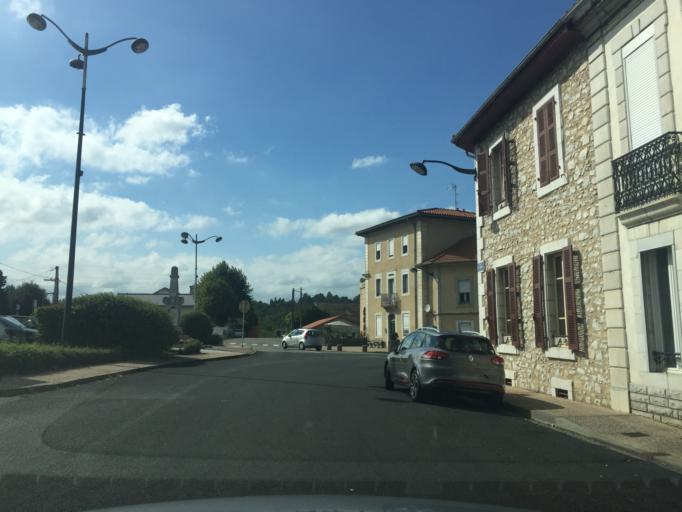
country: FR
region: Midi-Pyrenees
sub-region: Departement de la Haute-Garonne
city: Gourdan-Polignan
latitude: 43.0784
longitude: 0.5742
